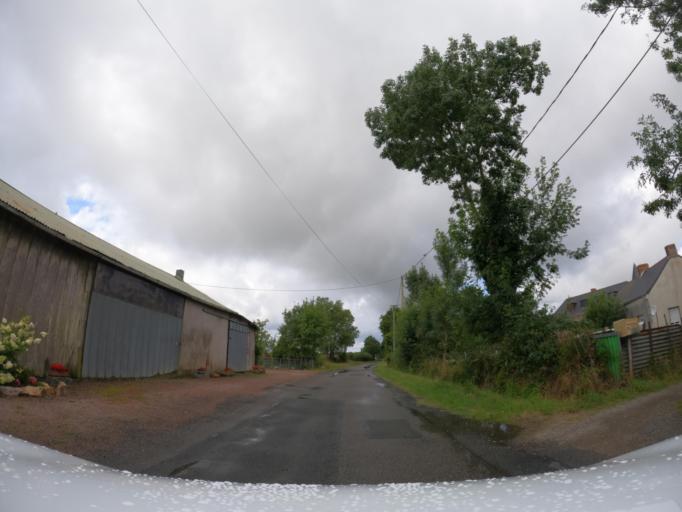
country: FR
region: Pays de la Loire
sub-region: Departement de la Loire-Atlantique
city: Ligne
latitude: 47.3936
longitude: -1.3848
